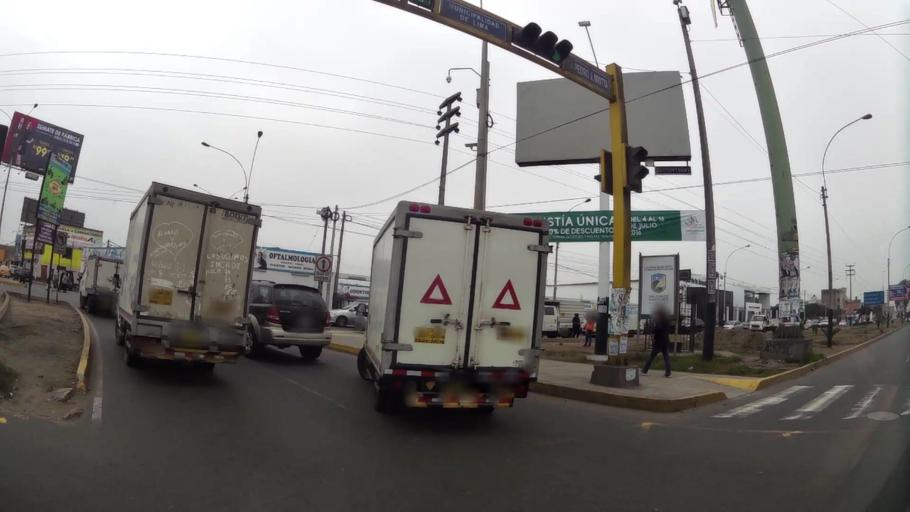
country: PE
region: Lima
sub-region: Lima
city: Surco
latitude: -12.1668
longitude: -76.9787
